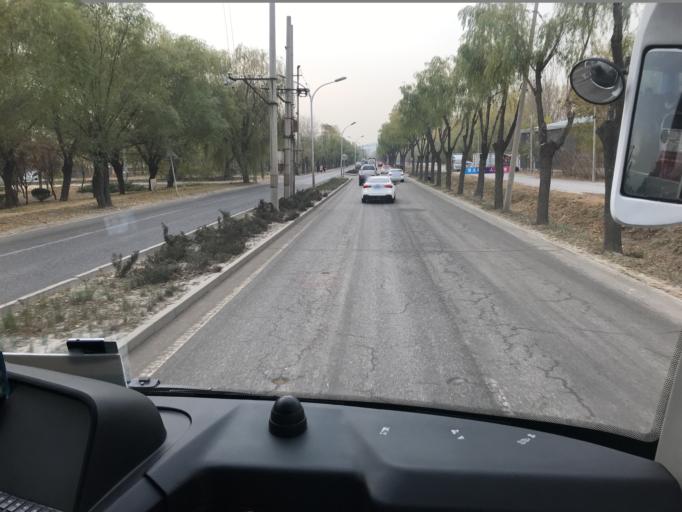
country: CN
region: Beijing
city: Wenquan
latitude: 40.0884
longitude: 116.2099
